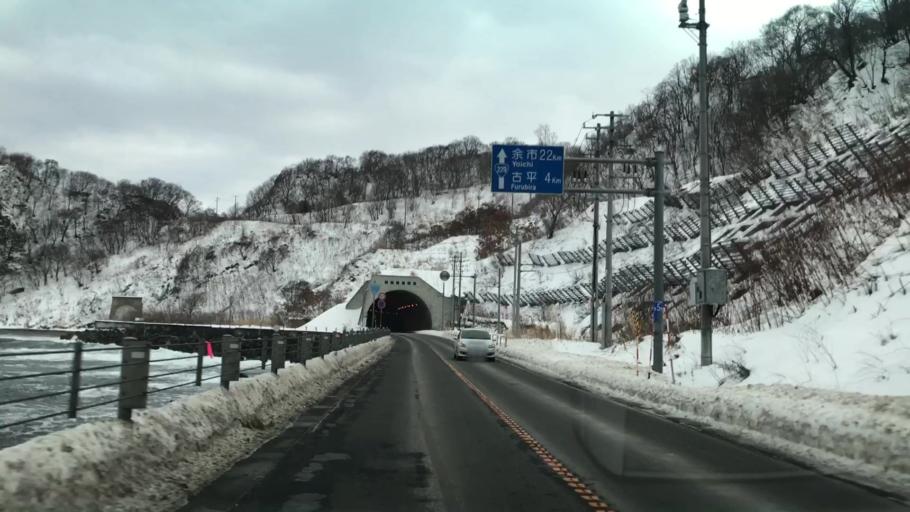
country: JP
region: Hokkaido
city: Yoichi
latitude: 43.2945
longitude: 140.6247
